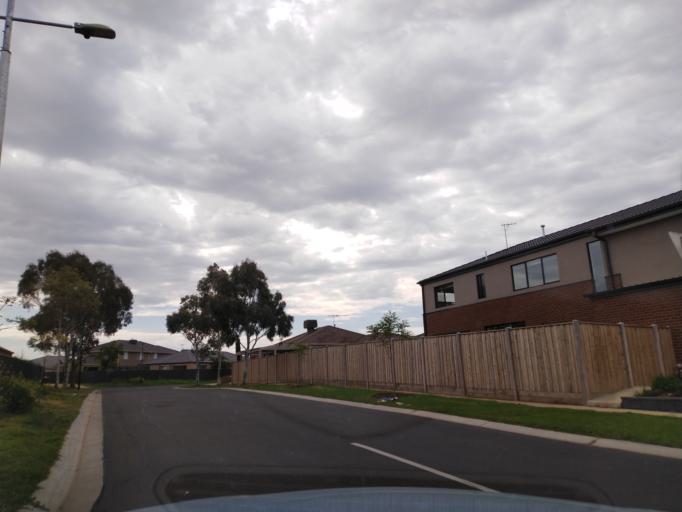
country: AU
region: Victoria
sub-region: Wyndham
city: Williams Landing
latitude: -37.8381
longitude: 144.7110
